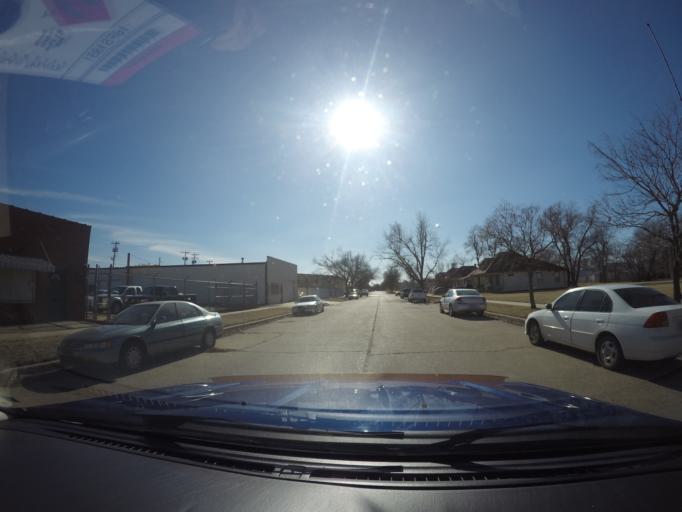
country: US
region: Kansas
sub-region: Sedgwick County
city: Wichita
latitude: 37.6875
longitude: -97.3507
